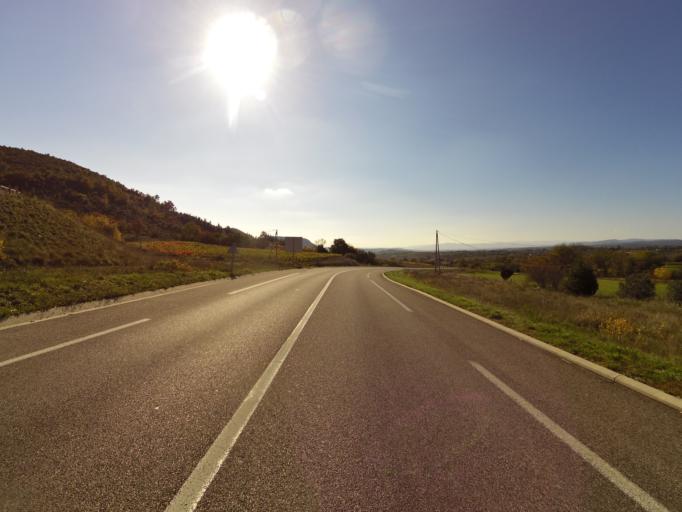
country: FR
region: Rhone-Alpes
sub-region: Departement de l'Ardeche
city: Lachapelle-sous-Aubenas
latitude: 44.5406
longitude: 4.3507
